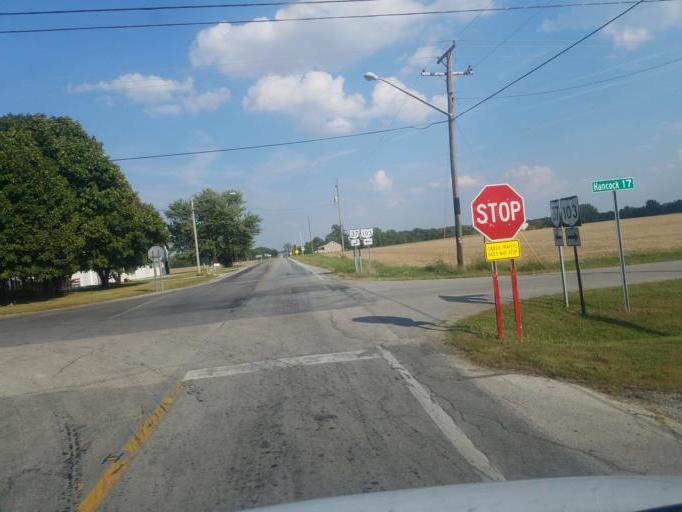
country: US
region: Ohio
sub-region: Hancock County
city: Arlington
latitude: 40.8910
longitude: -83.5570
